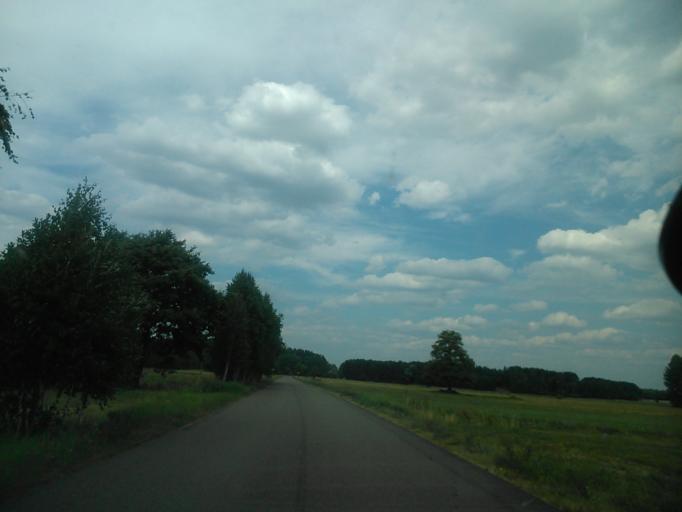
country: PL
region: Masovian Voivodeship
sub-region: Powiat ostrolecki
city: Czarnia
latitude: 53.3715
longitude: 21.2000
